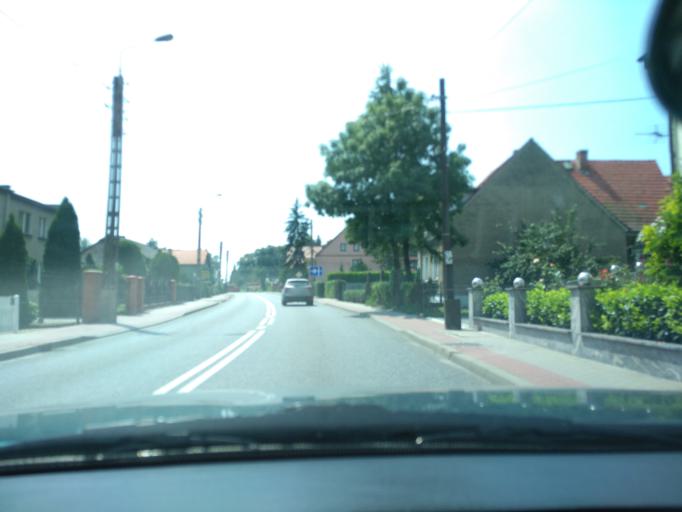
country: PL
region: Silesian Voivodeship
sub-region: Powiat raciborski
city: Raciborz
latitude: 50.0951
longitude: 18.2022
